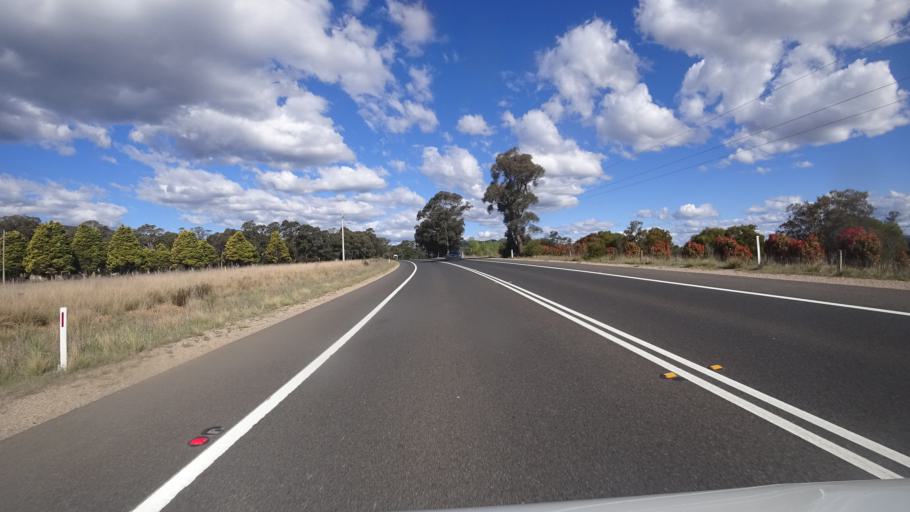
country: AU
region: New South Wales
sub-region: Lithgow
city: Bowenfels
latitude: -33.5555
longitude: 150.1913
